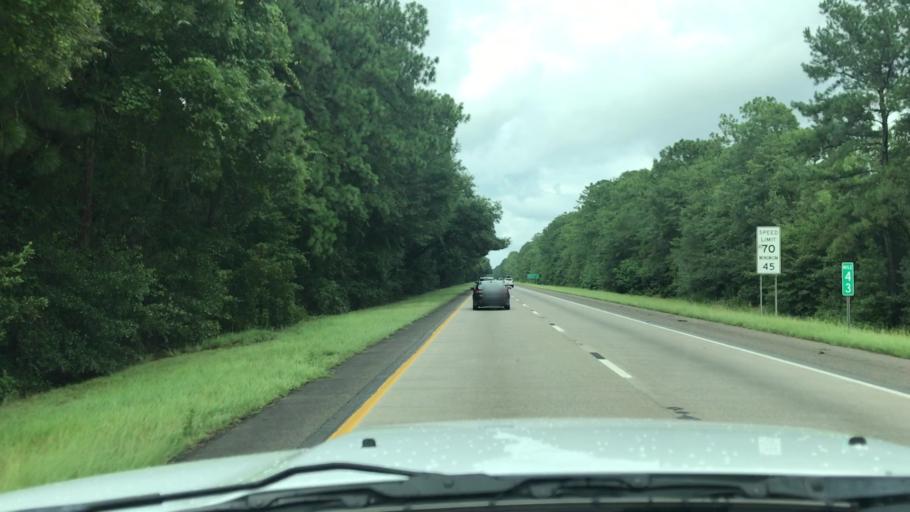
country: US
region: South Carolina
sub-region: Hampton County
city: Yemassee
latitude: 32.7579
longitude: -80.8203
